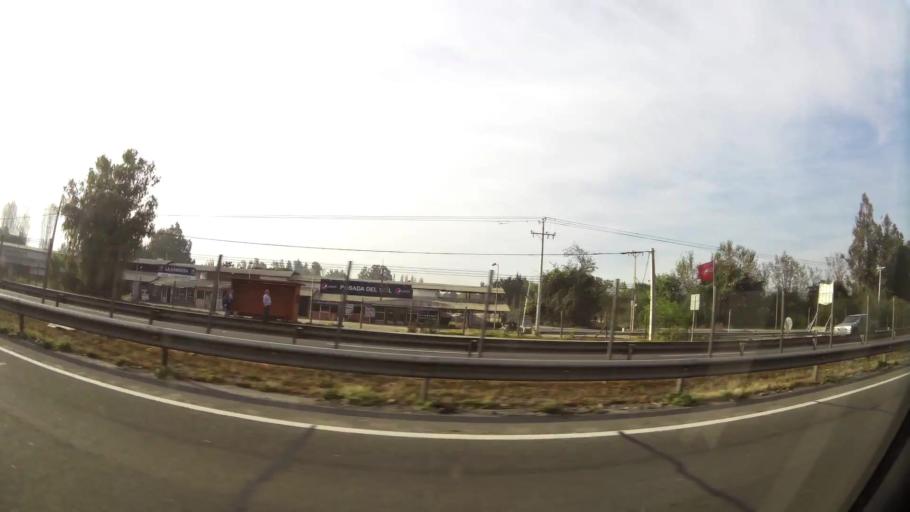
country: CL
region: Santiago Metropolitan
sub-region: Provincia de Talagante
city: Talagante
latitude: -33.6551
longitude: -70.8899
